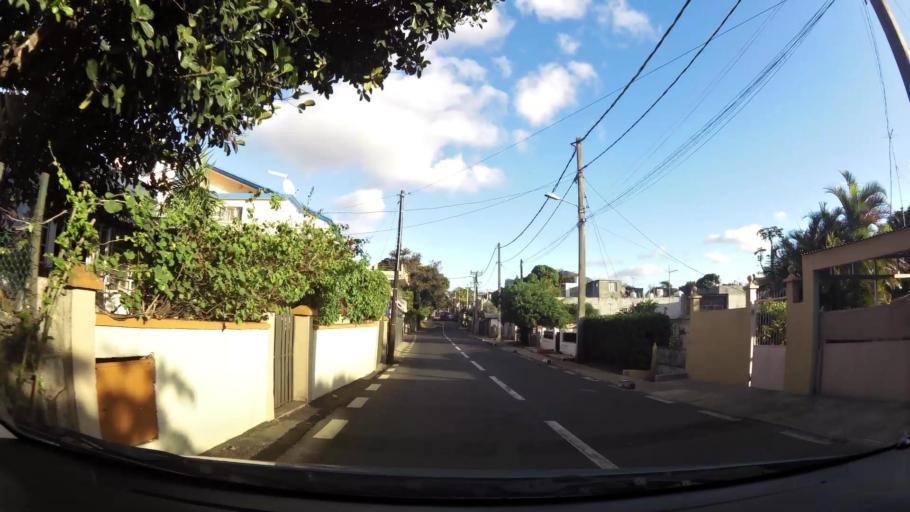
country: MU
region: Black River
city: Petite Riviere
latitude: -20.2223
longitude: 57.4636
